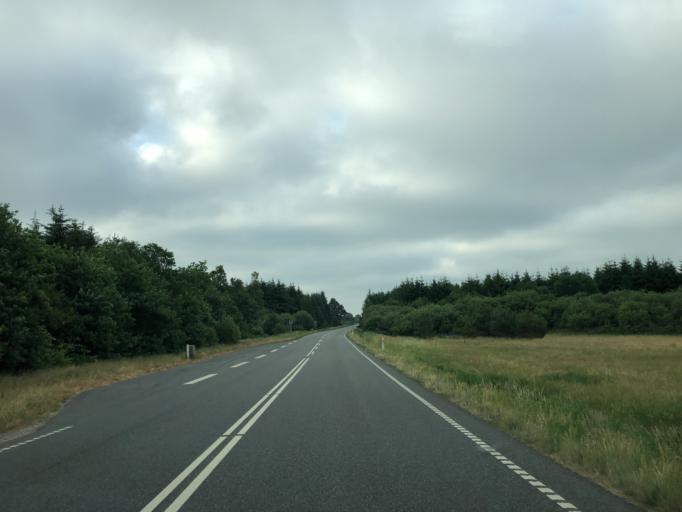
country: DK
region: Central Jutland
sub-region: Ikast-Brande Kommune
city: Brande
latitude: 55.9134
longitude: 9.1796
